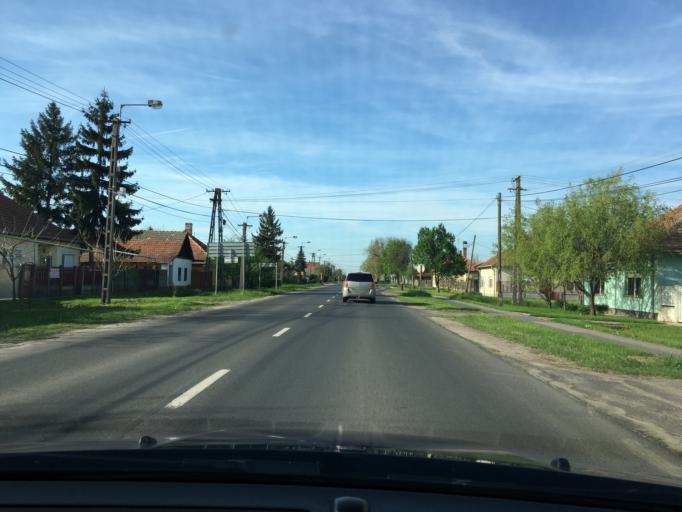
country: HU
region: Bekes
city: Mezobereny
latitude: 46.8366
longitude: 21.0276
